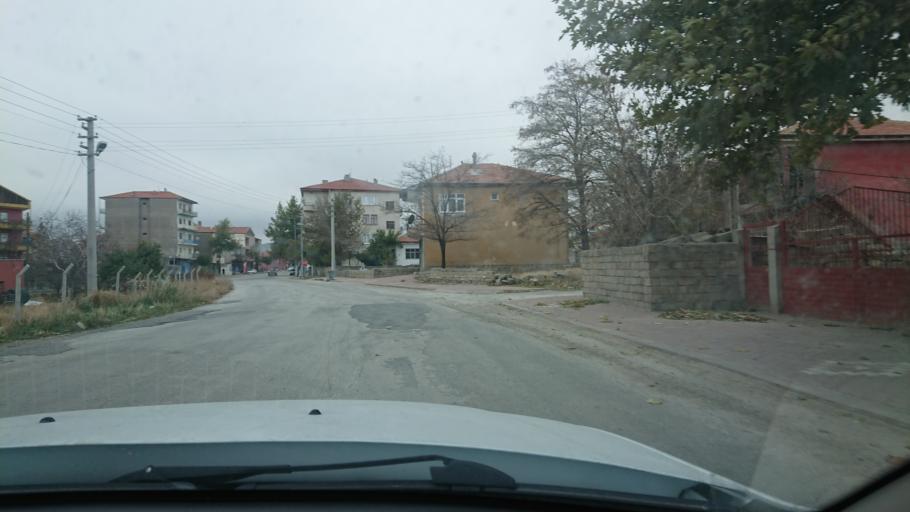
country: TR
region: Aksaray
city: Ortakoy
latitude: 38.7431
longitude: 34.0466
